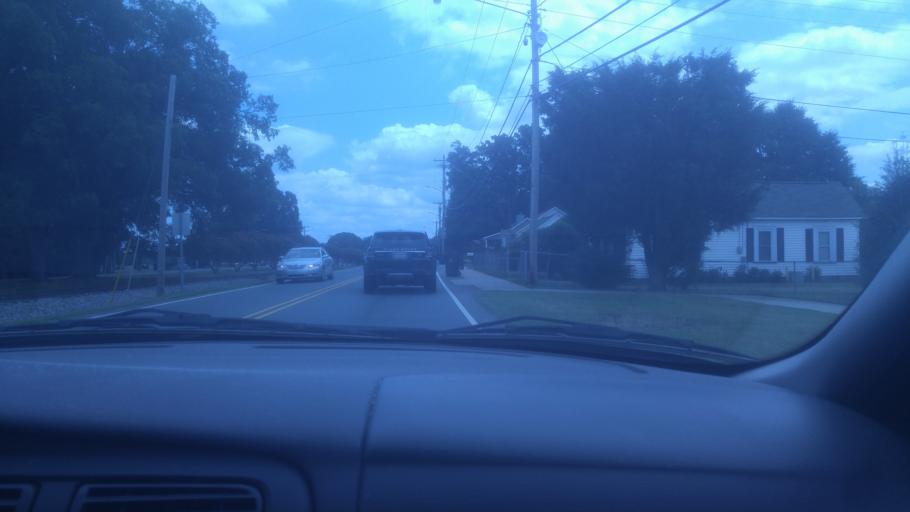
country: US
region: North Carolina
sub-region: Mecklenburg County
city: Cornelius
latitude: 35.4780
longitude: -80.8558
